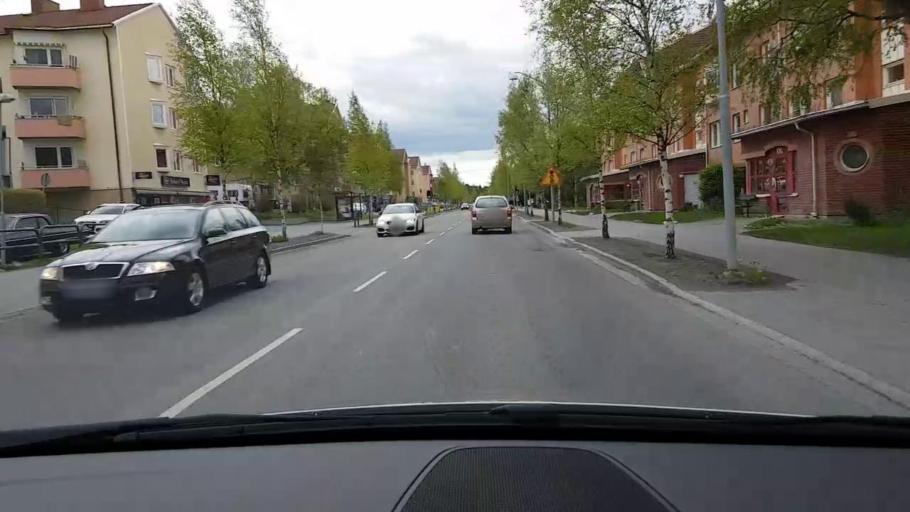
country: SE
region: Jaemtland
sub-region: OEstersunds Kommun
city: Ostersund
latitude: 63.1645
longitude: 14.6555
